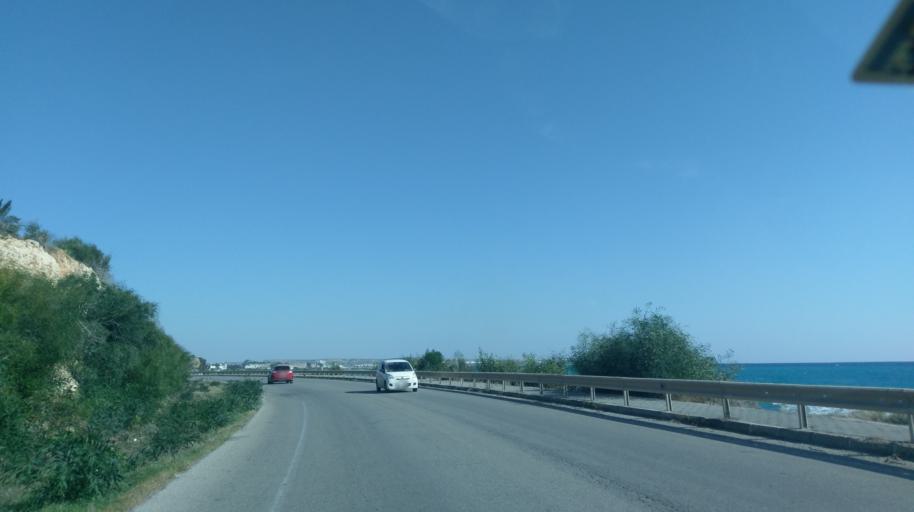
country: CY
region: Ammochostos
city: Trikomo
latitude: 35.3096
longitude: 33.9488
